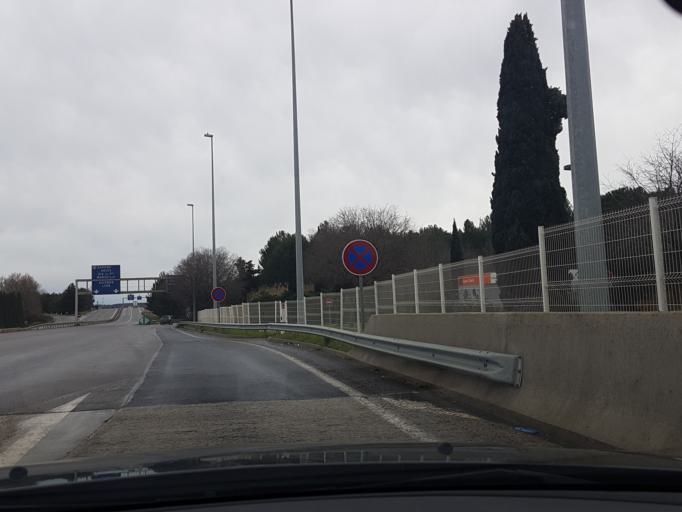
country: FR
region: Languedoc-Roussillon
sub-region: Departement du Gard
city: Nimes
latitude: 43.8135
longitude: 4.3428
